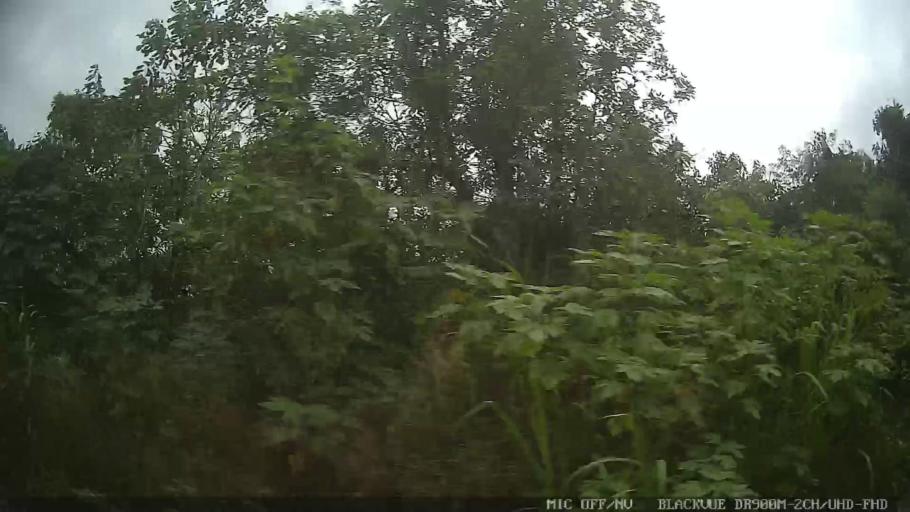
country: BR
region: Sao Paulo
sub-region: Aruja
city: Aruja
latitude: -23.4288
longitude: -46.2716
